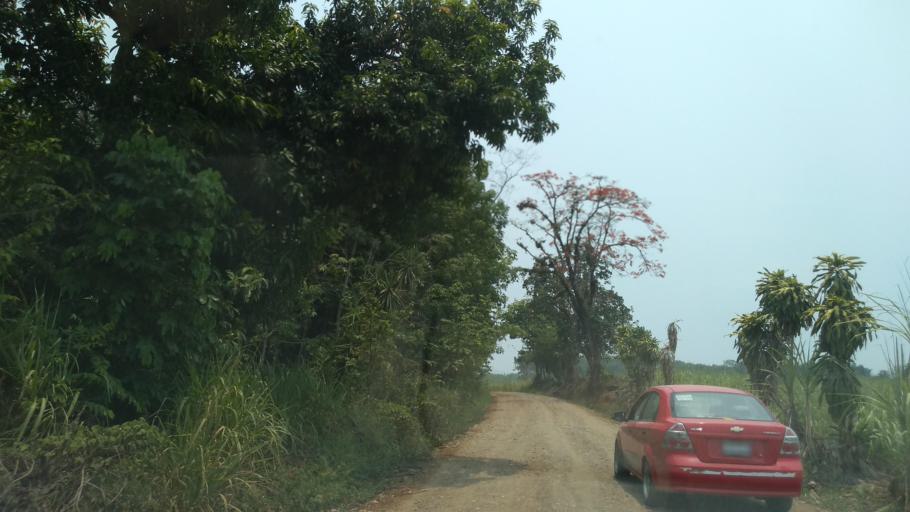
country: MX
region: Veracruz
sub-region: Tezonapa
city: Laguna Chica (Pueblo Nuevo)
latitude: 18.5055
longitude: -96.7713
